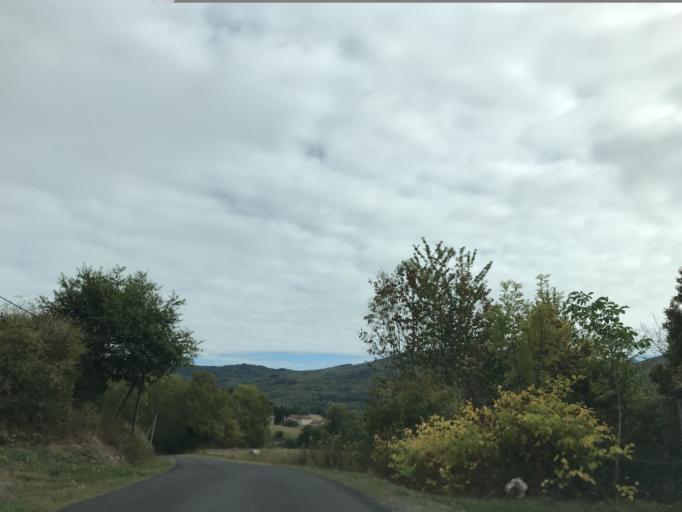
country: FR
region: Auvergne
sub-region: Departement du Puy-de-Dome
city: Escoutoux
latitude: 45.8229
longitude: 3.6069
